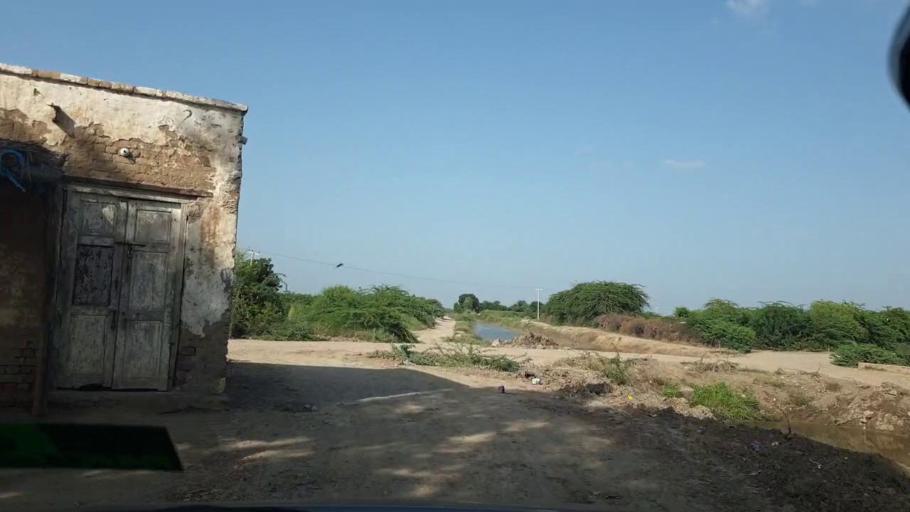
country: PK
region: Sindh
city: Naukot
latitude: 24.7114
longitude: 69.2067
